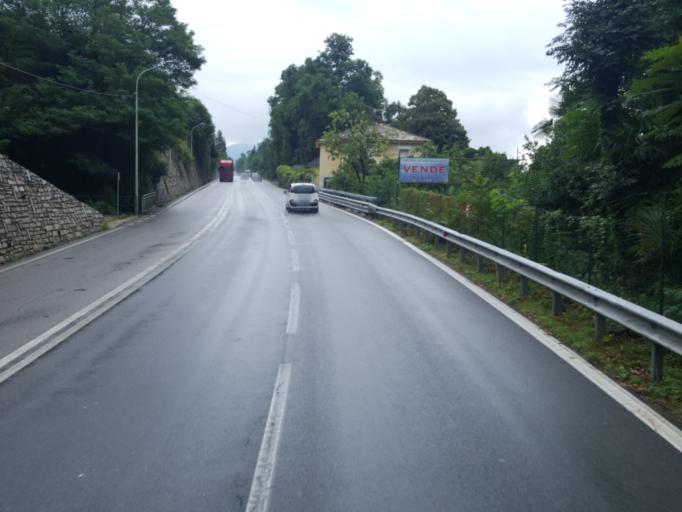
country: IT
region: Piedmont
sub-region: Provincia Verbano-Cusio-Ossola
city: Verbania
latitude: 45.9338
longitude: 8.5317
